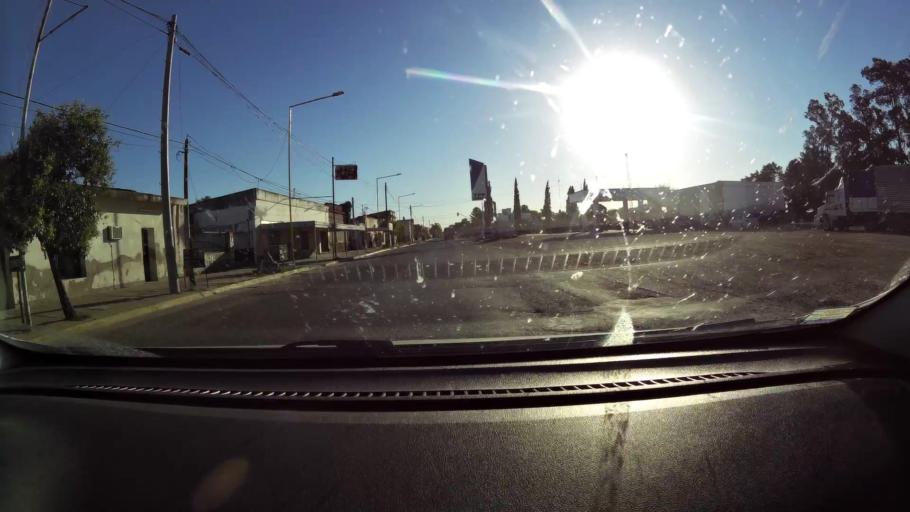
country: AR
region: Cordoba
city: Saturnino M. Laspiur
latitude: -31.7020
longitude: -62.4796
